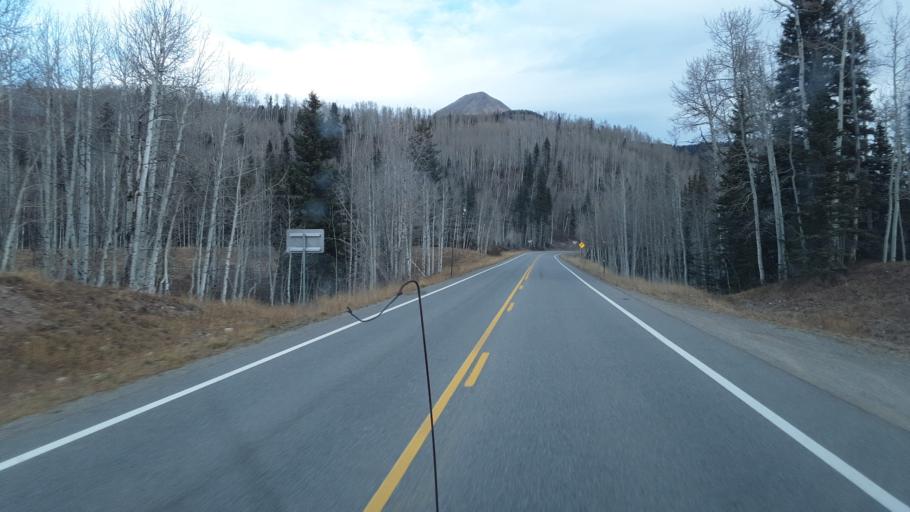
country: US
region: Colorado
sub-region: San Juan County
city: Silverton
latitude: 37.6621
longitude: -107.7979
